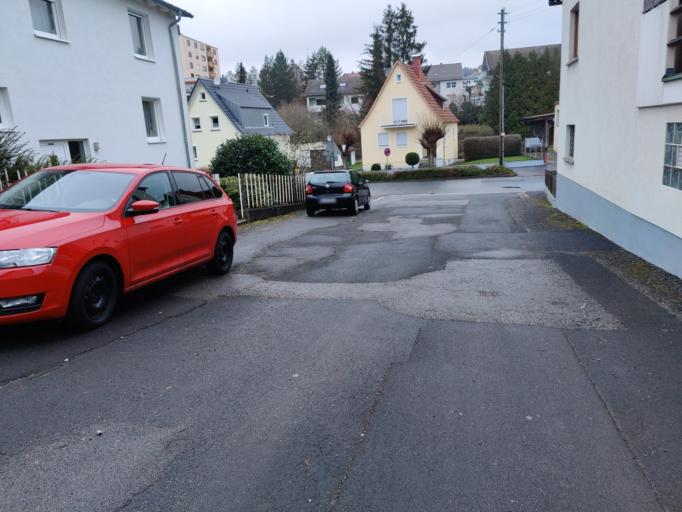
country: DE
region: Bavaria
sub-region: Regierungsbezirk Unterfranken
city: Bad Kissingen
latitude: 50.2036
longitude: 10.0962
